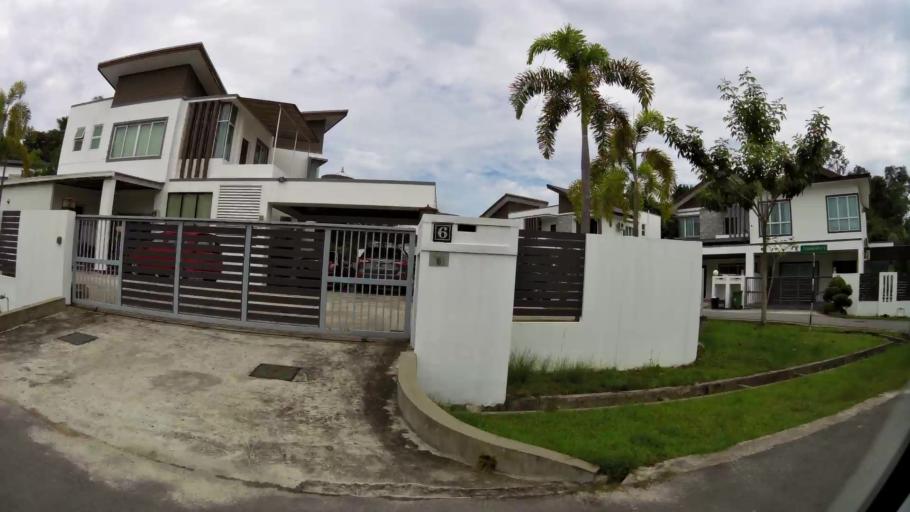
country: BN
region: Brunei and Muara
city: Bandar Seri Begawan
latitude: 4.8899
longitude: 114.8997
